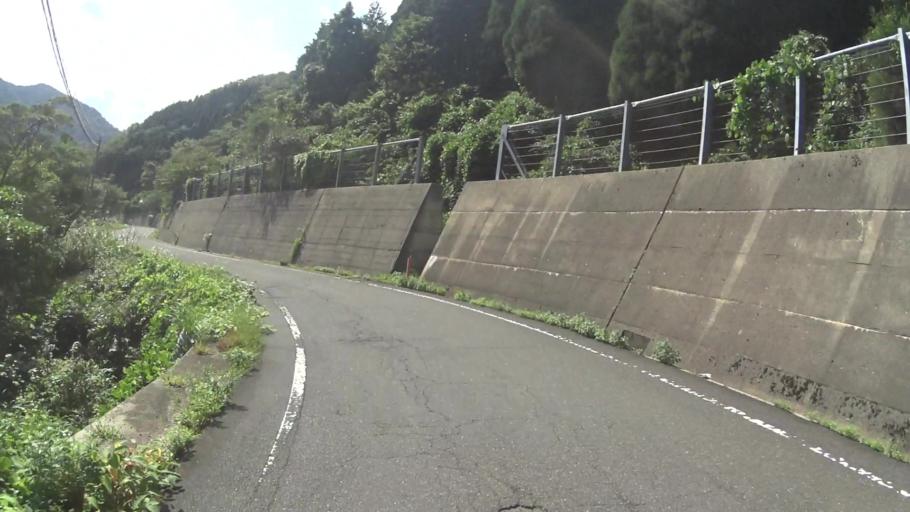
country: JP
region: Kyoto
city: Miyazu
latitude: 35.7042
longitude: 135.1882
